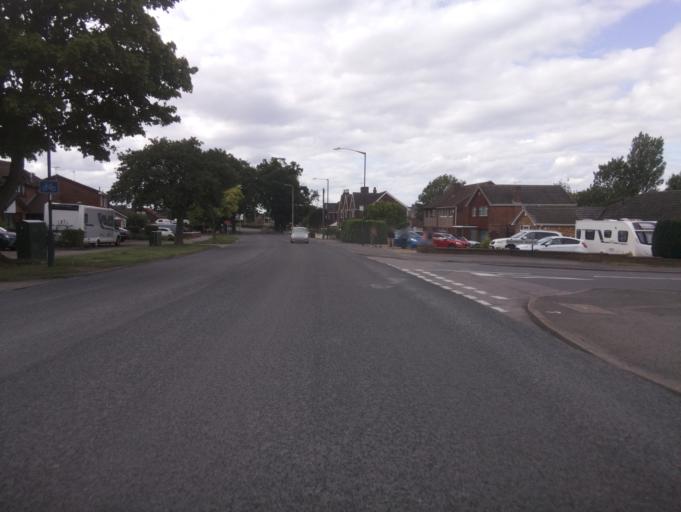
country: GB
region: England
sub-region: Warwickshire
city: Nuneaton
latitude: 52.5386
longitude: -1.4659
